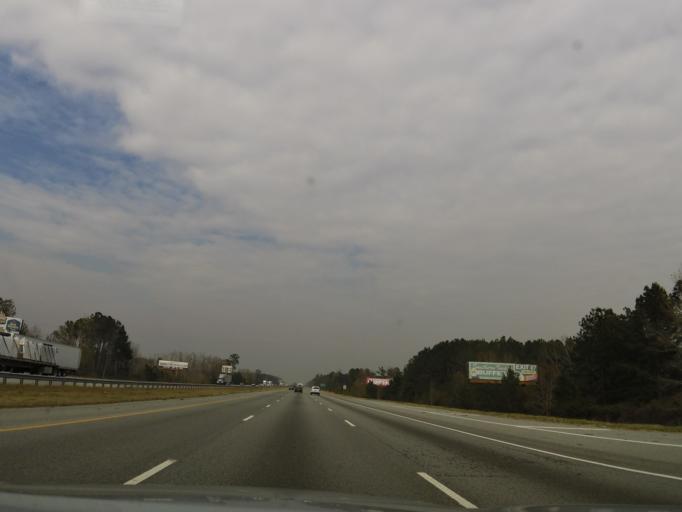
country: US
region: Georgia
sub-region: Liberty County
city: Midway
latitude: 31.6611
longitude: -81.3926
